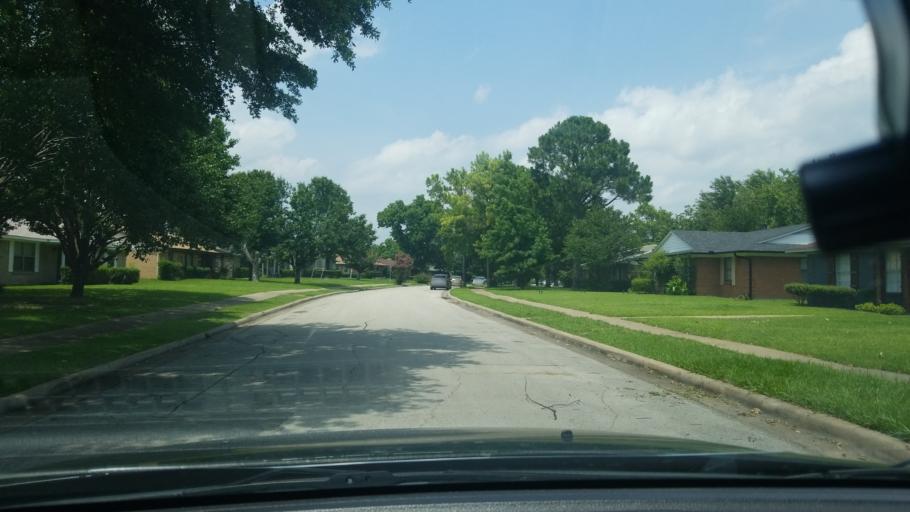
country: US
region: Texas
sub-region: Dallas County
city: Mesquite
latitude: 32.7998
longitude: -96.6401
